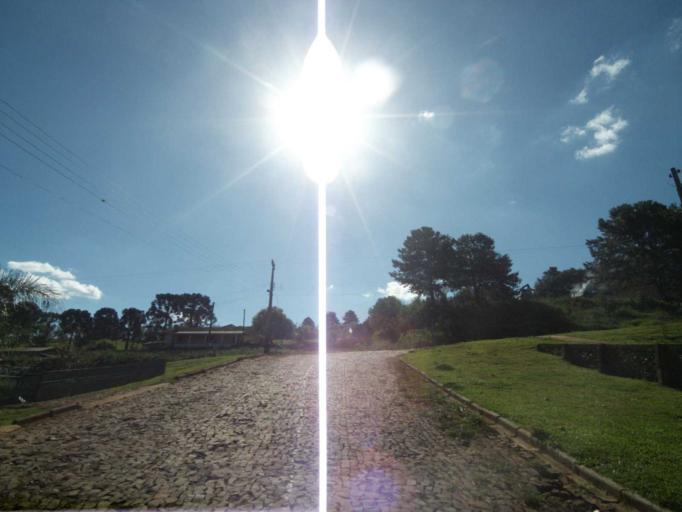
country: BR
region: Parana
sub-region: Laranjeiras Do Sul
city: Laranjeiras do Sul
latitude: -25.3851
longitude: -52.2052
